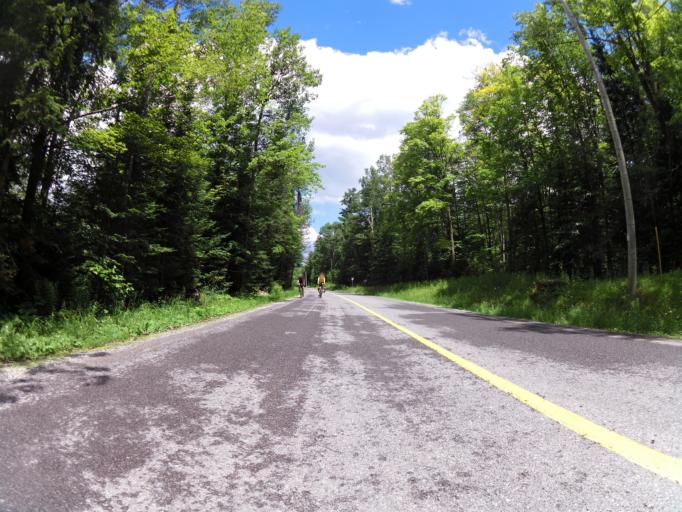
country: CA
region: Ontario
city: Renfrew
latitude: 45.0535
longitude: -76.6715
